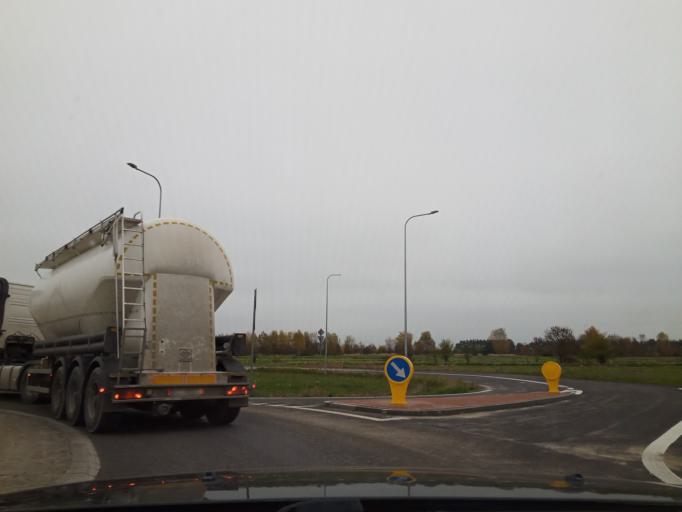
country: PL
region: Swietokrzyskie
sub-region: Powiat jedrzejowski
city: Jedrzejow
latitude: 50.6188
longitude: 20.3126
